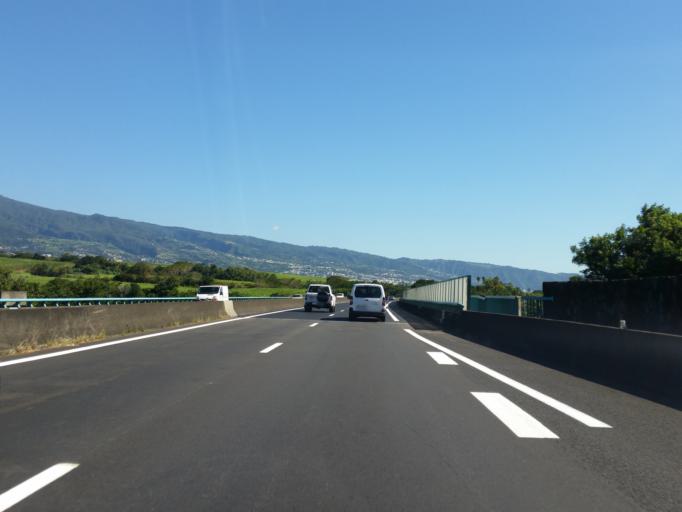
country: RE
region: Reunion
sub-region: Reunion
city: Sainte-Marie
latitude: -20.9025
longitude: 55.5565
